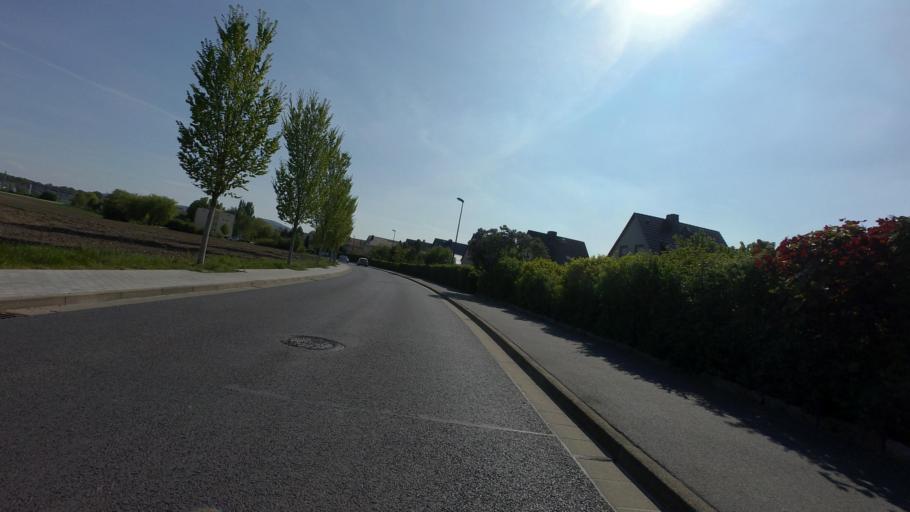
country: DE
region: Saxony
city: Kamenz
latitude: 51.2802
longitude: 14.1160
